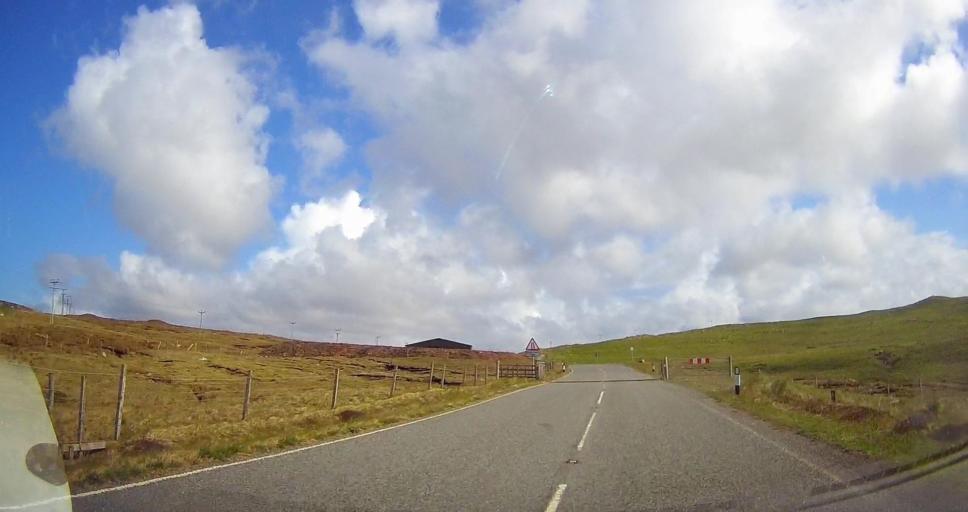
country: GB
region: Scotland
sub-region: Shetland Islands
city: Lerwick
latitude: 60.4765
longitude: -1.4077
